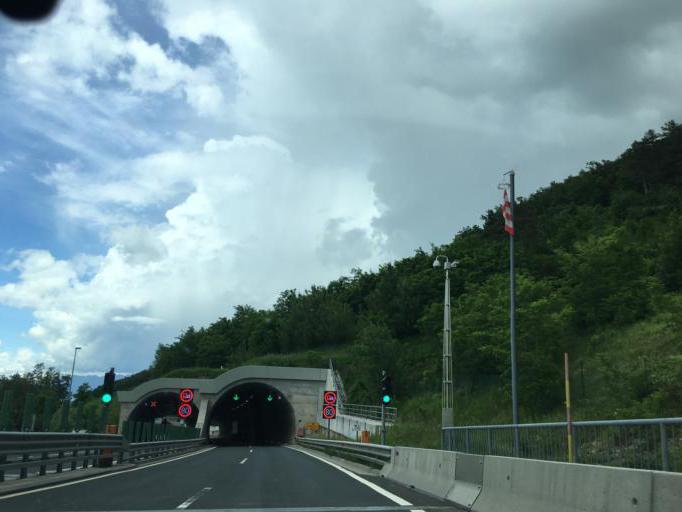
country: SI
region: Vipava
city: Vipava
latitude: 45.7689
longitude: 14.0310
